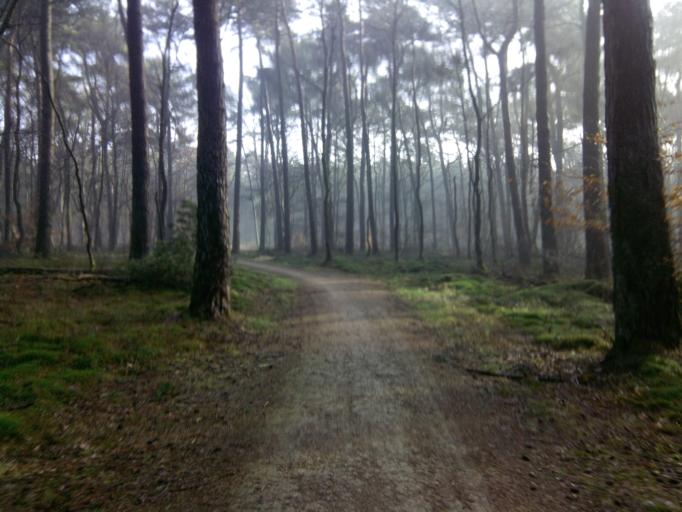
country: NL
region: Utrecht
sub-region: Gemeente Utrechtse Heuvelrug
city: Maarsbergen
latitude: 52.0379
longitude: 5.3889
